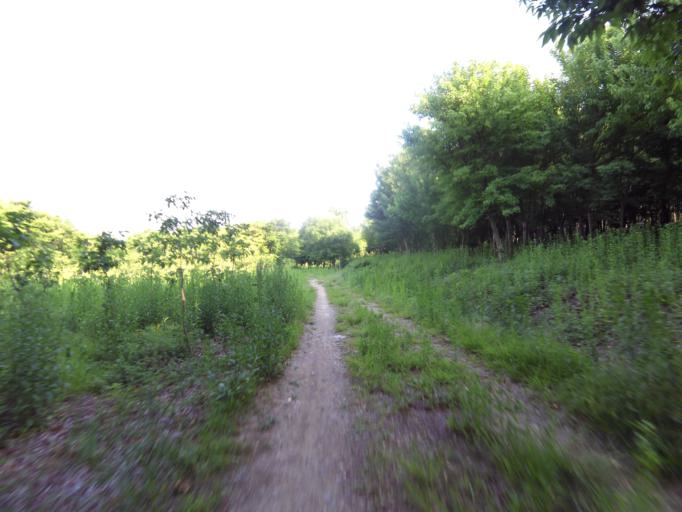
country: KR
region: Gyeongsangbuk-do
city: Gyeongsan-si
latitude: 35.8380
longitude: 128.7610
